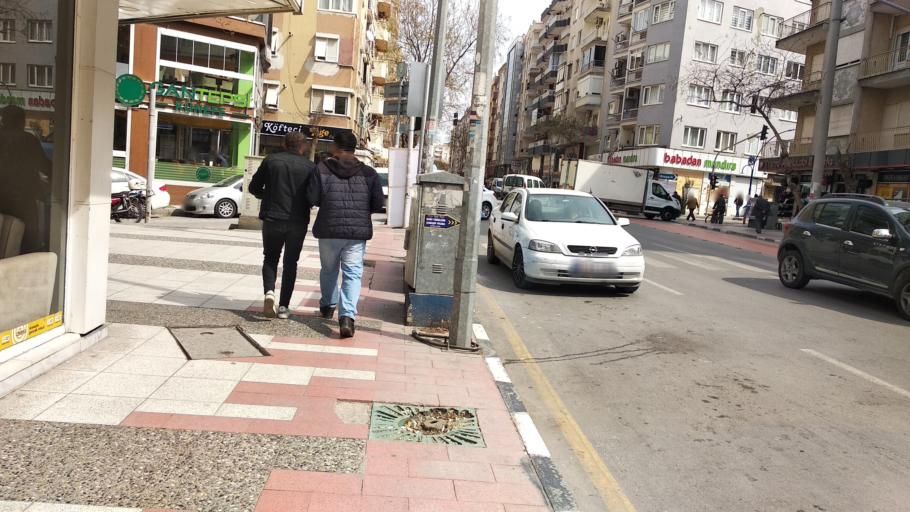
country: TR
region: Manisa
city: Manisa
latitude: 38.6134
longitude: 27.4173
